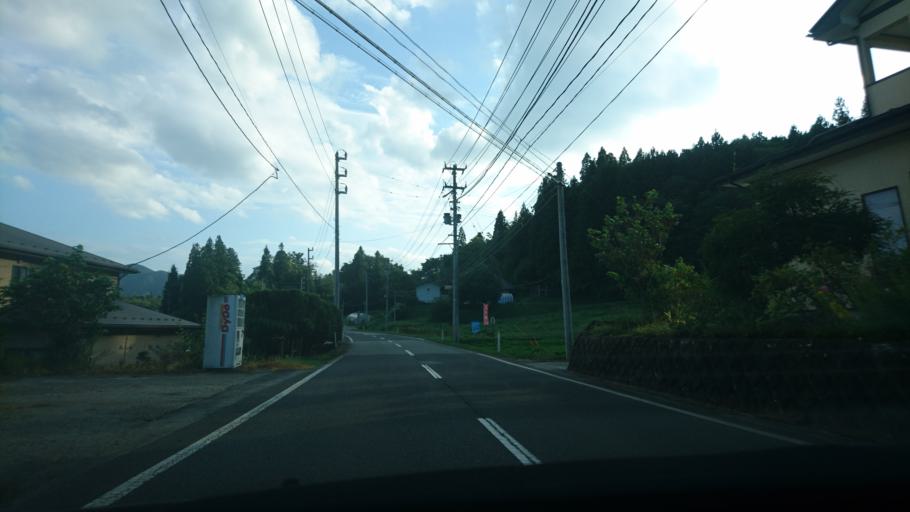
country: JP
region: Iwate
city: Ichinoseki
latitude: 39.0014
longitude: 141.2815
